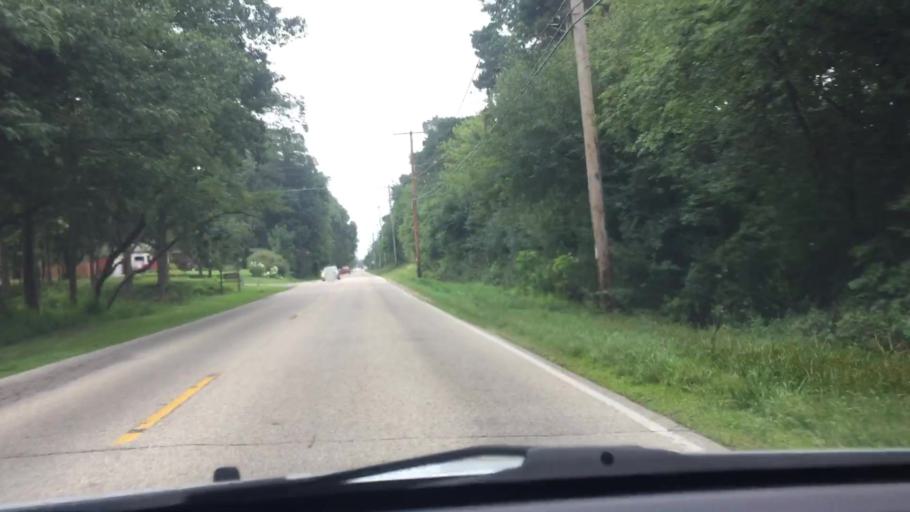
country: US
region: Wisconsin
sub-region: Waukesha County
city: Delafield
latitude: 43.0535
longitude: -88.4424
